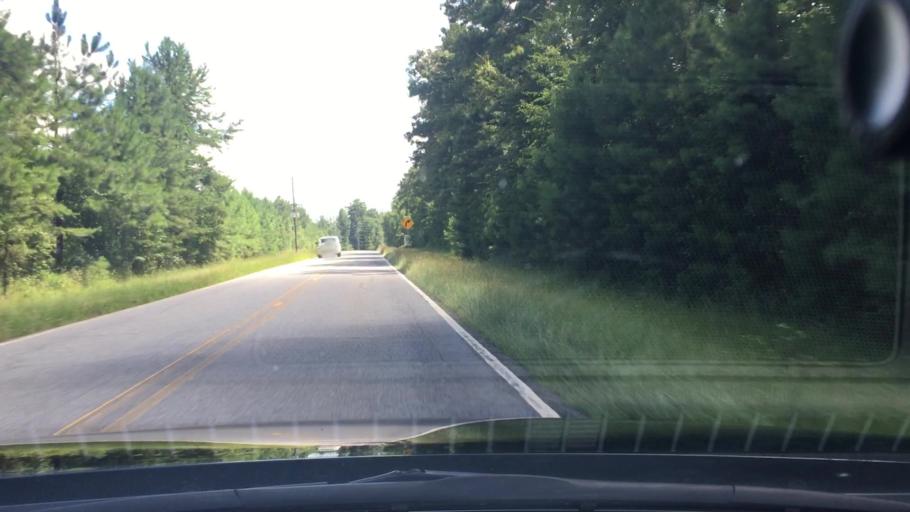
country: US
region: Georgia
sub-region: Putnam County
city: Jefferson
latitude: 33.3632
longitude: -83.2544
